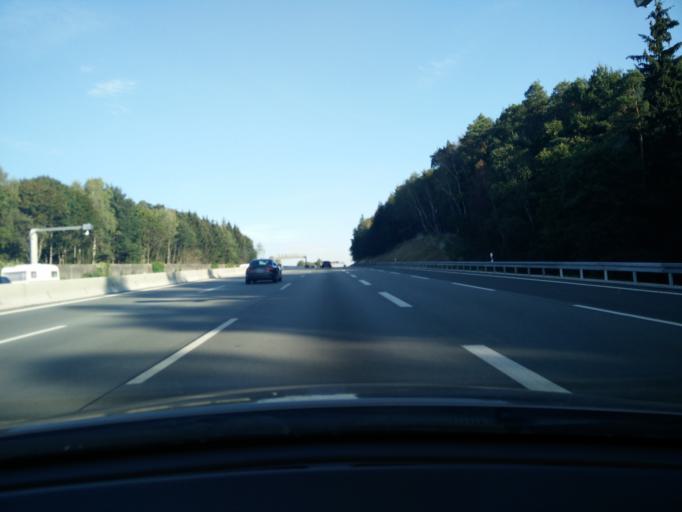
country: DE
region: Bavaria
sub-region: Upper Bavaria
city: Paunzhausen
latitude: 48.4682
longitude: 11.5872
